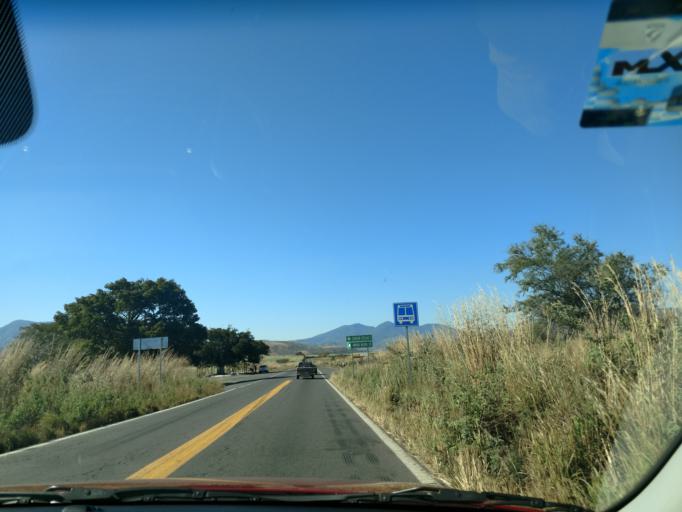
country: MX
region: Nayarit
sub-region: Ahuacatlan
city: Ahuacatlan
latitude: 21.1289
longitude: -104.6014
